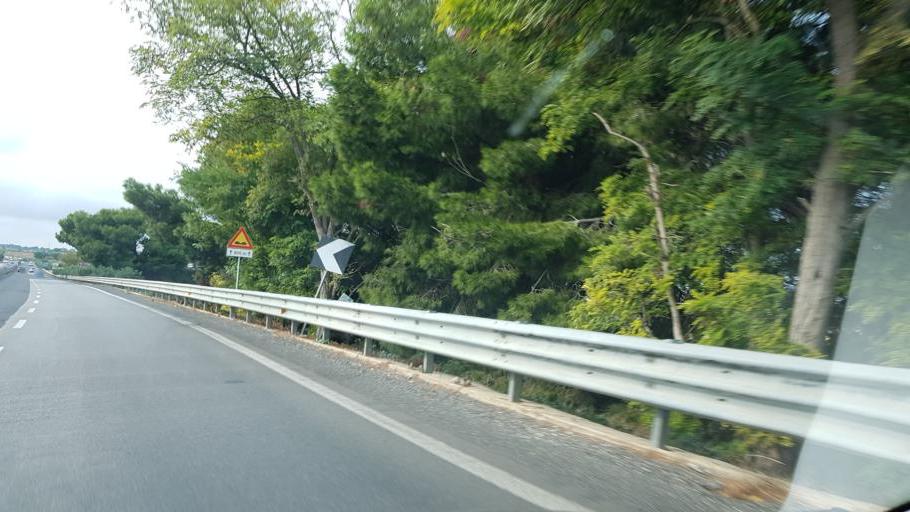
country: IT
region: Apulia
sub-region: Provincia di Bari
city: Mola di Bari
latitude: 41.0499
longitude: 17.0910
